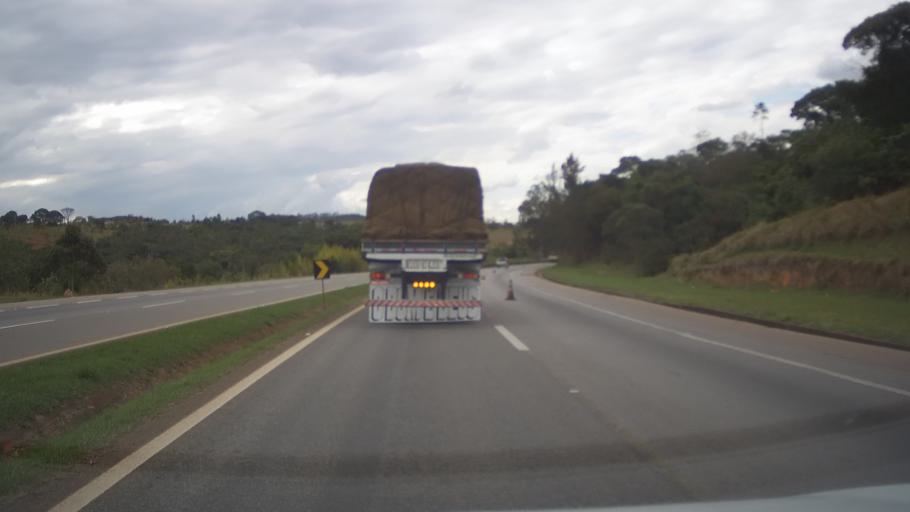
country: BR
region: Minas Gerais
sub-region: Itauna
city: Itauna
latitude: -20.3278
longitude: -44.4554
